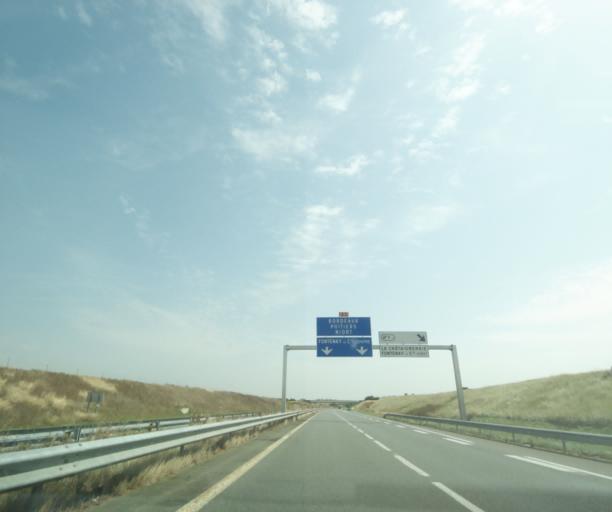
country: FR
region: Pays de la Loire
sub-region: Departement de la Vendee
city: Serigne
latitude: 46.4606
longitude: -0.8867
